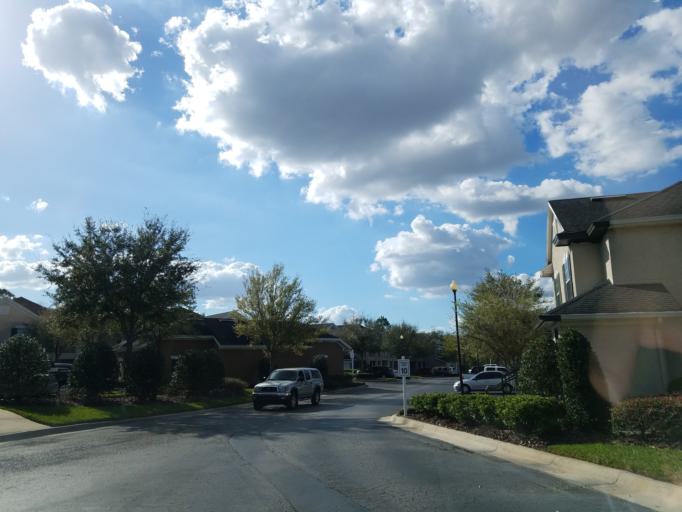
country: US
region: Florida
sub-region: Hillsborough County
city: Pebble Creek
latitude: 28.1872
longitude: -82.3671
